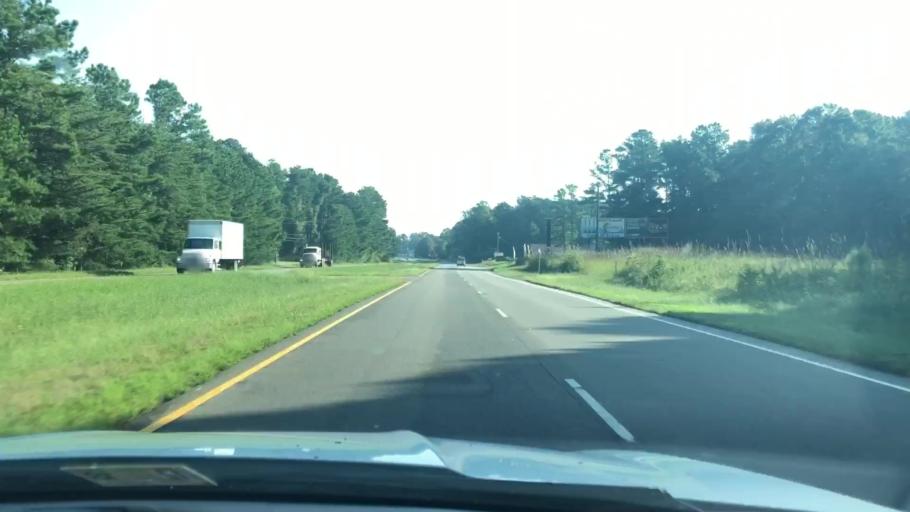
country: US
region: Virginia
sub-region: King William County
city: West Point
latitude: 37.5155
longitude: -76.8377
